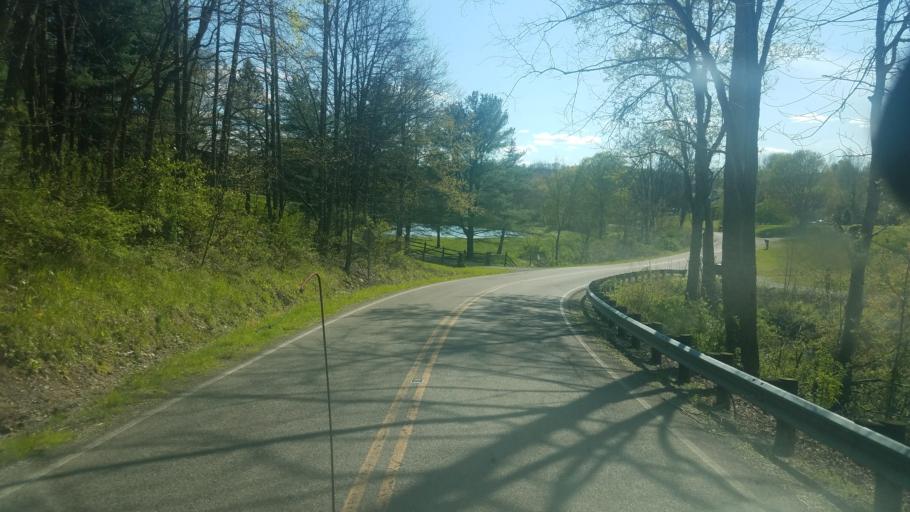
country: US
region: Ohio
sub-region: Coshocton County
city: Coshocton
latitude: 40.3339
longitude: -81.8925
